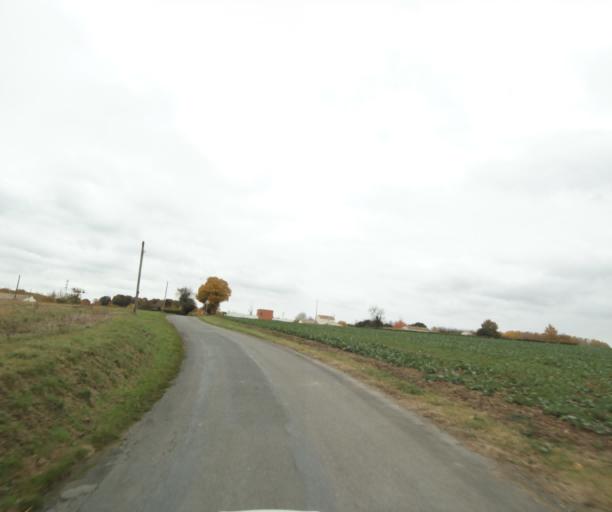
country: FR
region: Poitou-Charentes
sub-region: Departement de la Charente-Maritime
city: Bussac-sur-Charente
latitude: 45.7726
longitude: -0.6435
